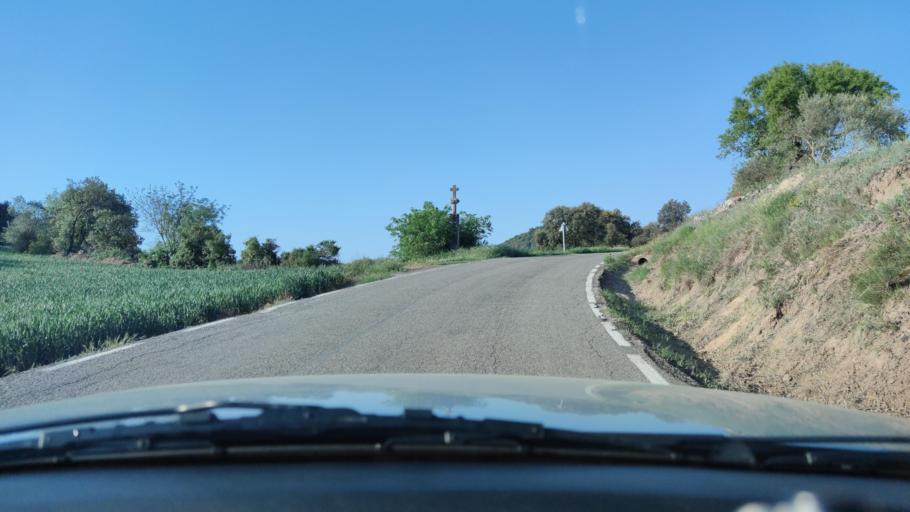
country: ES
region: Catalonia
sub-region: Provincia de Lleida
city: Artesa de Segre
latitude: 41.8830
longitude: 1.0213
